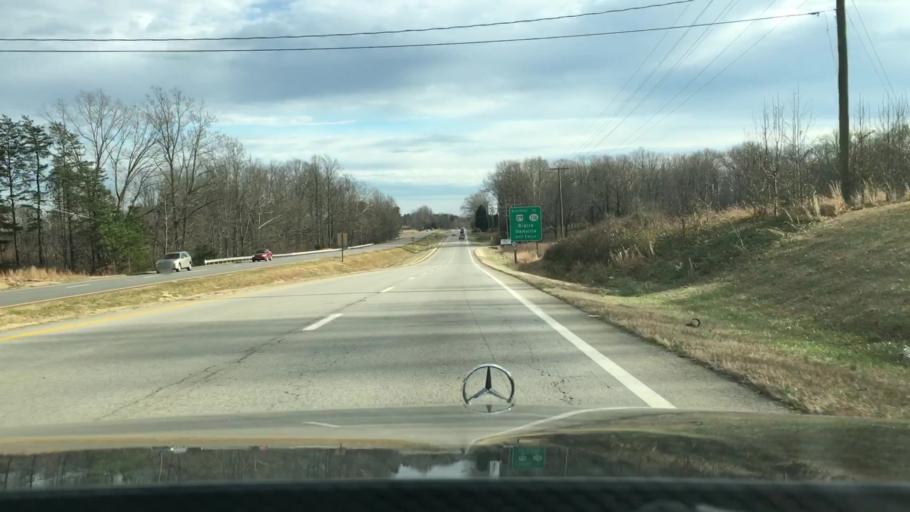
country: US
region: Virginia
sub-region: Pittsylvania County
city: Mount Hermon
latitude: 36.7173
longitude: -79.3803
